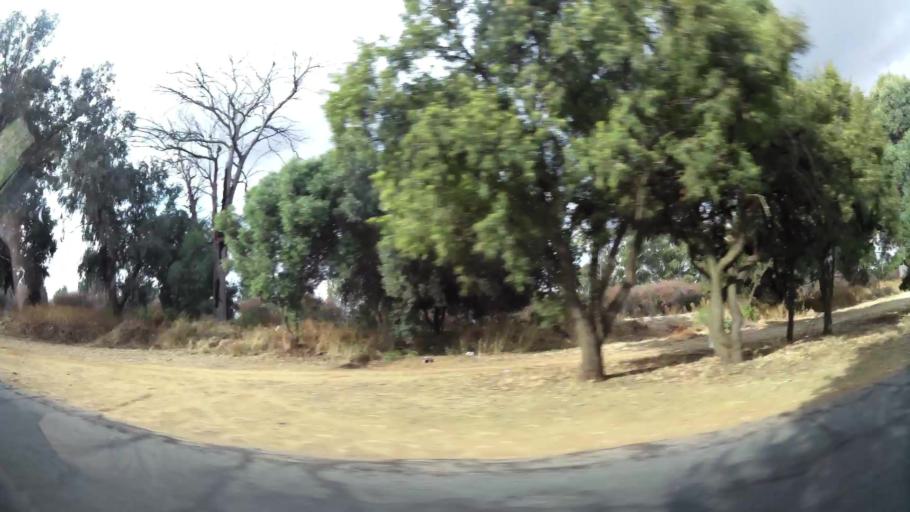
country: ZA
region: Orange Free State
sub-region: Fezile Dabi District Municipality
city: Sasolburg
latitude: -26.8110
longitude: 27.8384
